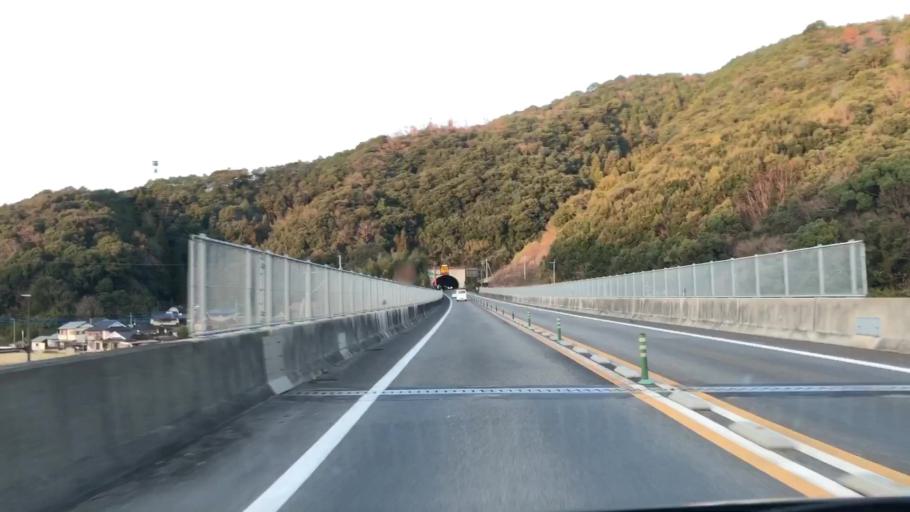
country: JP
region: Kumamoto
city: Minamata
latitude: 32.3011
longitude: 130.5103
